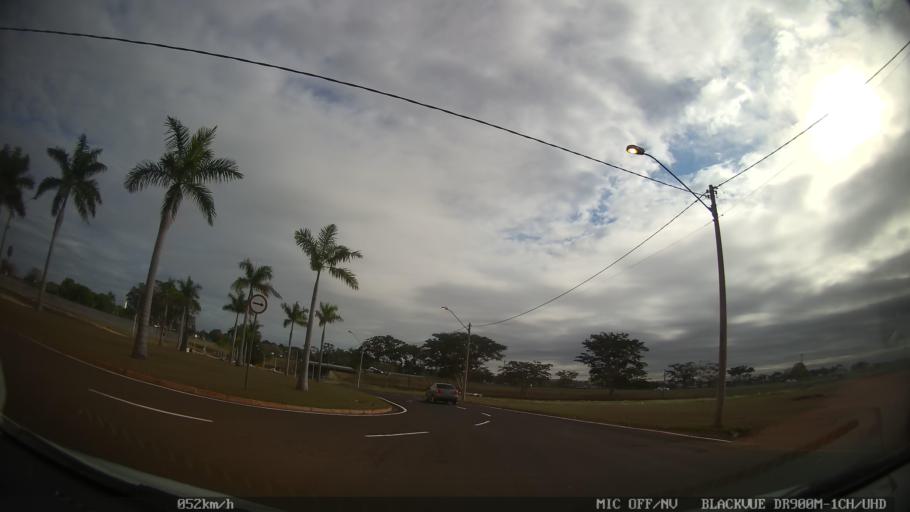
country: BR
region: Sao Paulo
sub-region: Sao Jose Do Rio Preto
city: Sao Jose do Rio Preto
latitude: -20.8244
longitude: -49.4178
